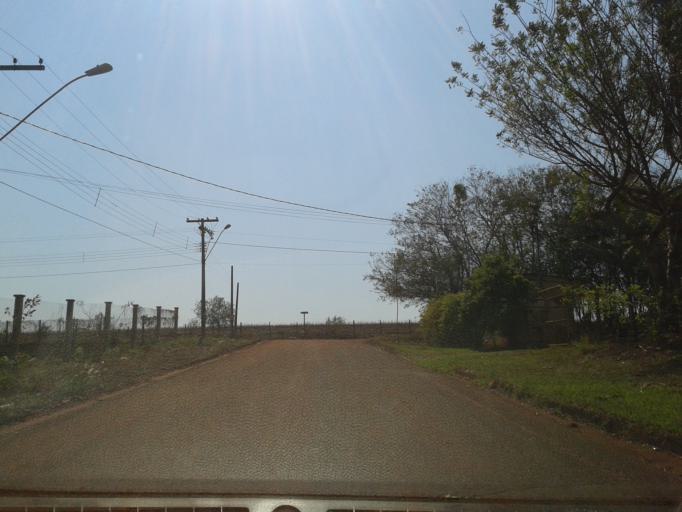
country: BR
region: Minas Gerais
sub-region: Ituiutaba
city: Ituiutaba
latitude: -18.9539
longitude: -49.4537
